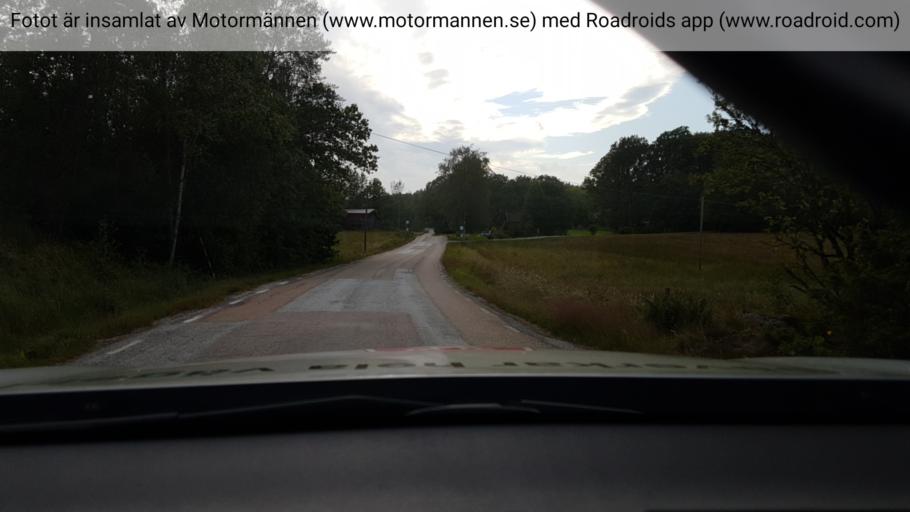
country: SE
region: Vaestra Goetaland
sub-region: Orust
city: Henan
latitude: 58.1601
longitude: 11.6737
